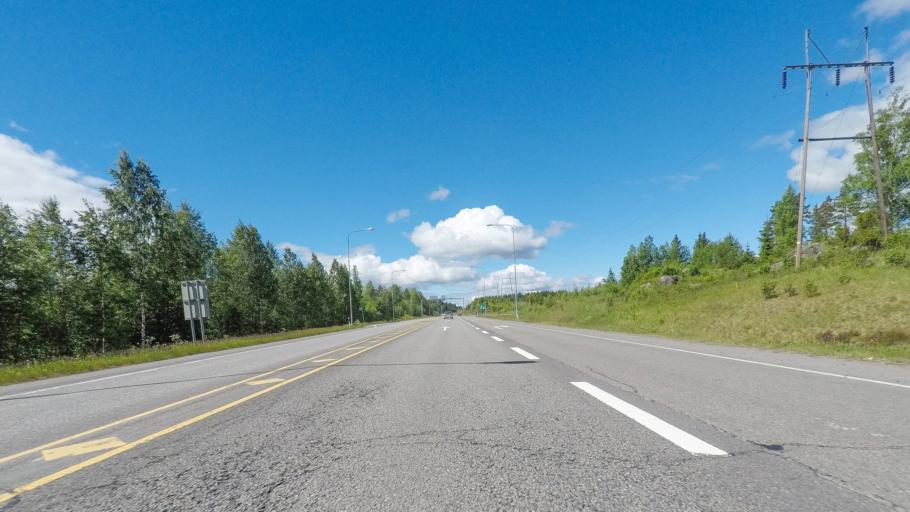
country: FI
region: Paijanne Tavastia
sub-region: Lahti
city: Heinola
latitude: 61.2999
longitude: 26.0638
